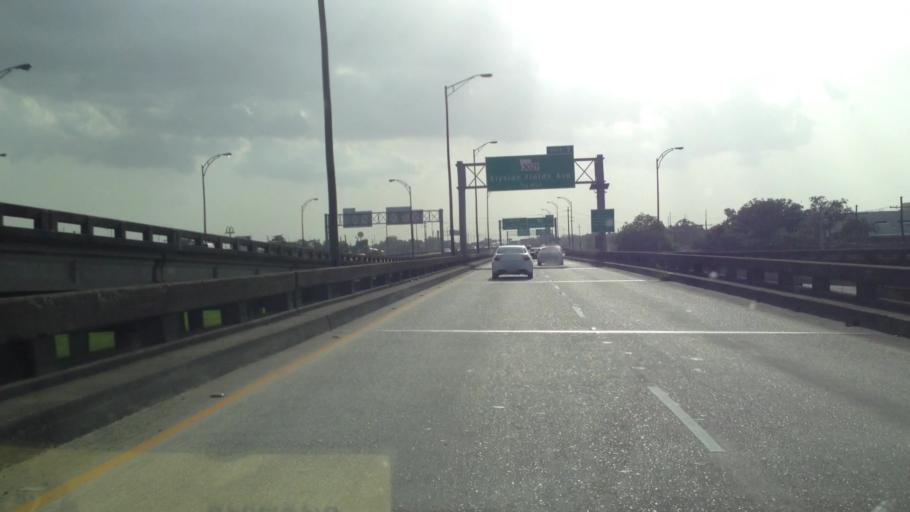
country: US
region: Louisiana
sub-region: Orleans Parish
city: New Orleans
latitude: 29.9919
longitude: -90.0512
